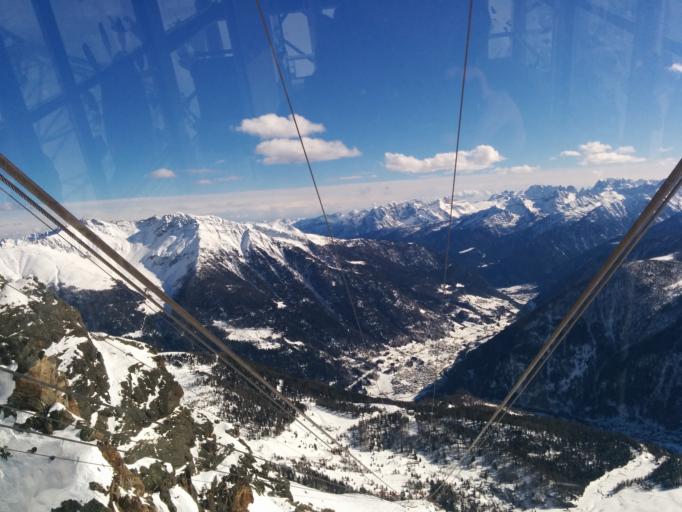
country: IT
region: Trentino-Alto Adige
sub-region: Provincia di Trento
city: Cogolo
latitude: 46.3806
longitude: 10.6373
